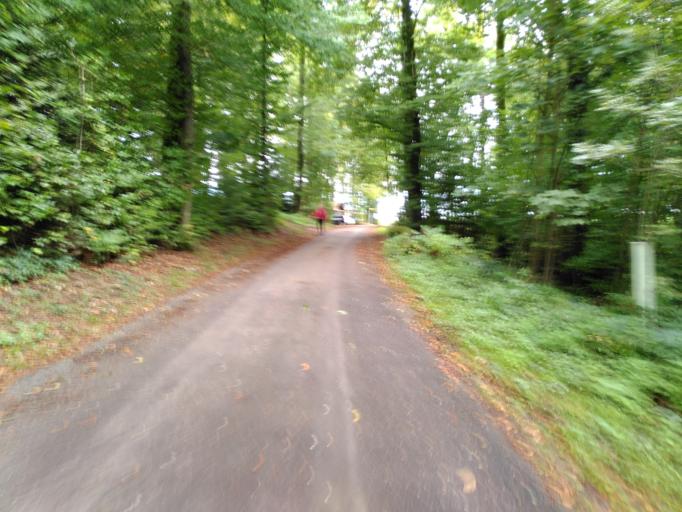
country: CH
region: Bern
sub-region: Emmental District
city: Ersigen
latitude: 47.0976
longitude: 7.6089
